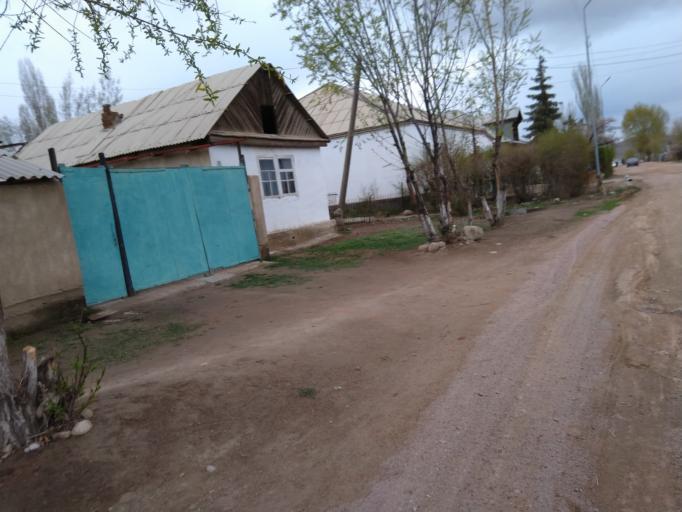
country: KG
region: Ysyk-Koel
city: Bokombayevskoye
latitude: 42.1111
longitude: 76.9829
